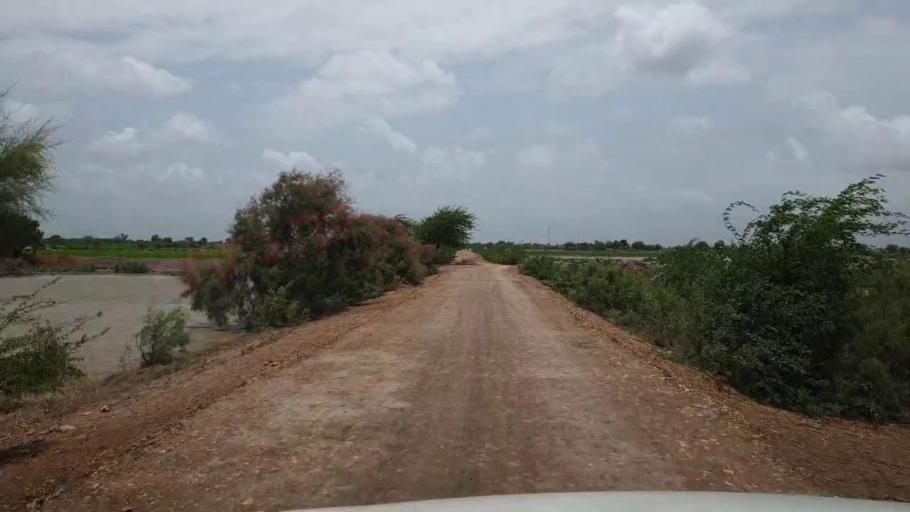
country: PK
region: Sindh
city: Kario
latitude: 24.7197
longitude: 68.5744
